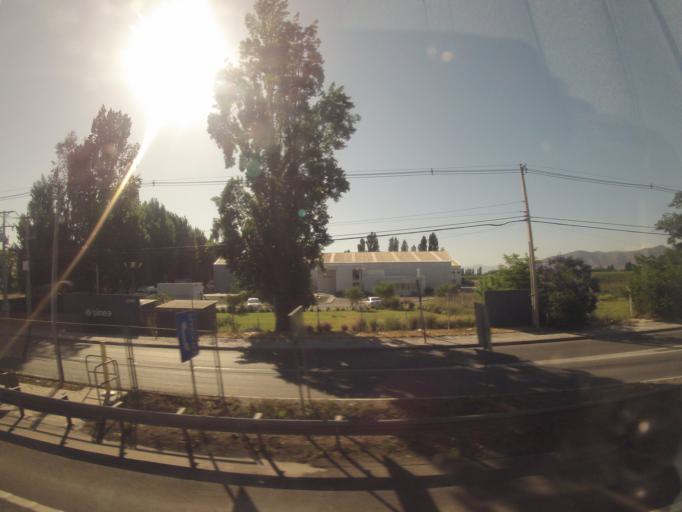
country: CL
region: Santiago Metropolitan
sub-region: Provincia de Maipo
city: San Bernardo
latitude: -33.6527
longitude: -70.7140
